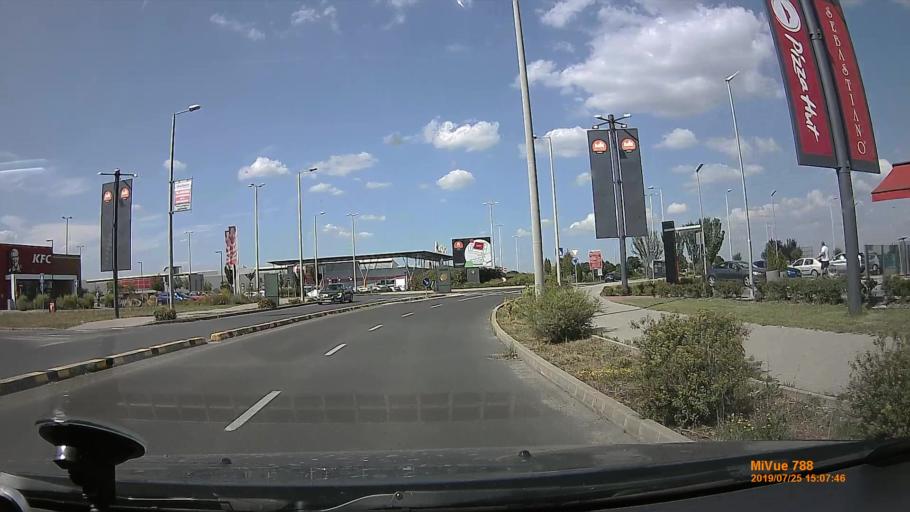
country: HU
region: Borsod-Abauj-Zemplen
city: Felsozsolca
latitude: 48.1067
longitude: 20.8374
